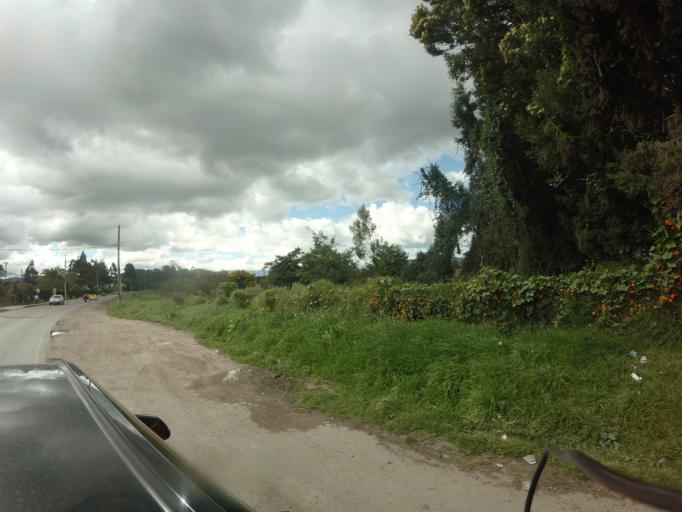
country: CO
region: Cundinamarca
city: Sopo
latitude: 4.9159
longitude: -73.9444
